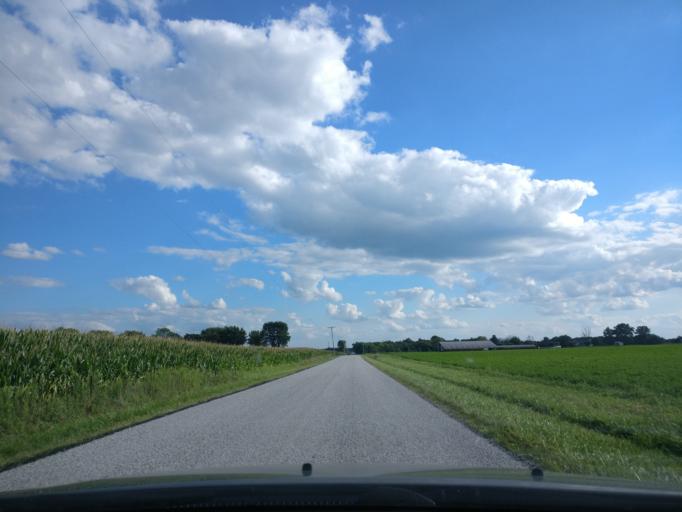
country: US
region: Ohio
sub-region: Clinton County
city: Wilmington
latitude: 39.4940
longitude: -83.7854
